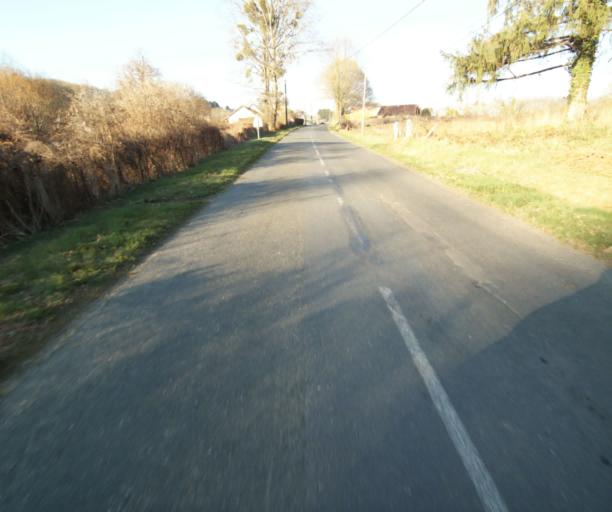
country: FR
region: Limousin
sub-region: Departement de la Correze
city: Saint-Clement
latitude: 45.3471
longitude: 1.6249
